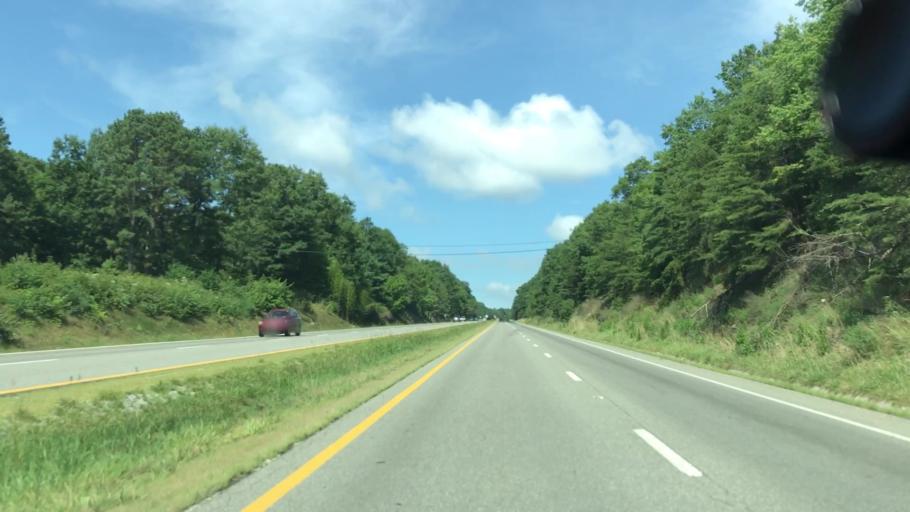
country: US
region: Virginia
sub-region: Montgomery County
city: Blacksburg
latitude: 37.2780
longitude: -80.4259
